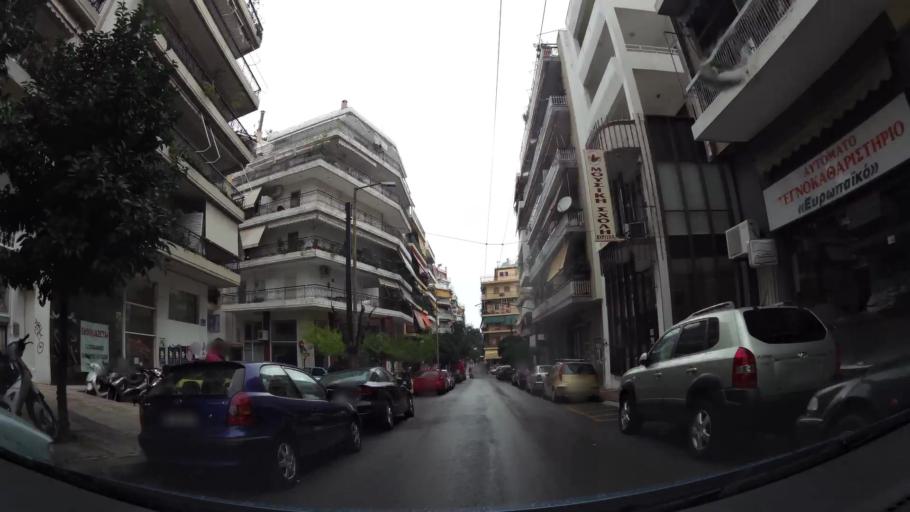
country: GR
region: Attica
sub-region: Nomarchia Athinas
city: Vyronas
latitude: 37.9587
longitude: 23.7569
